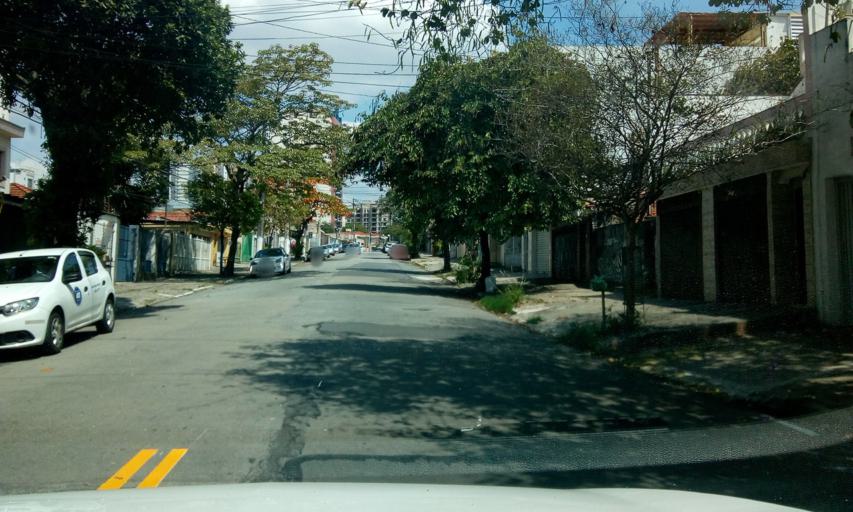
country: BR
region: Sao Paulo
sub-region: Sao Paulo
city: Sao Paulo
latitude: -23.5324
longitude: -46.7063
